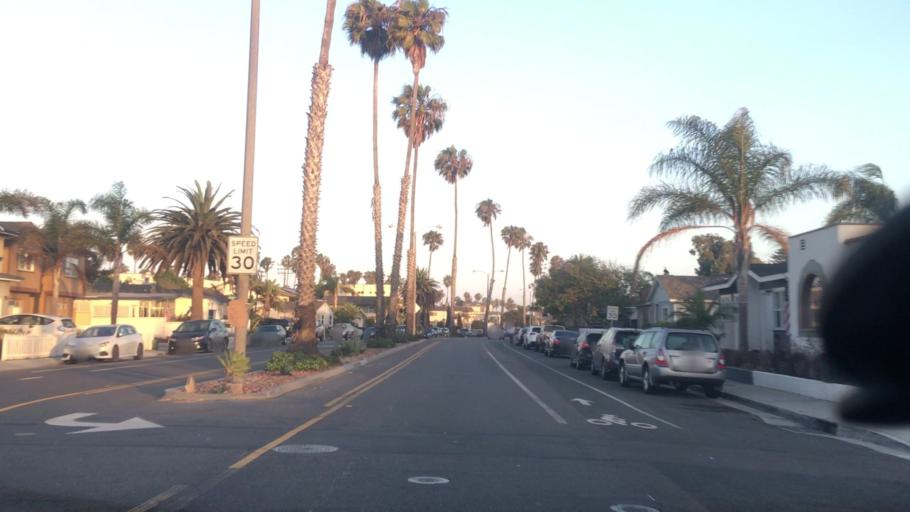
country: US
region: California
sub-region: Ventura County
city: Ventura
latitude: 34.2639
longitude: -119.2719
